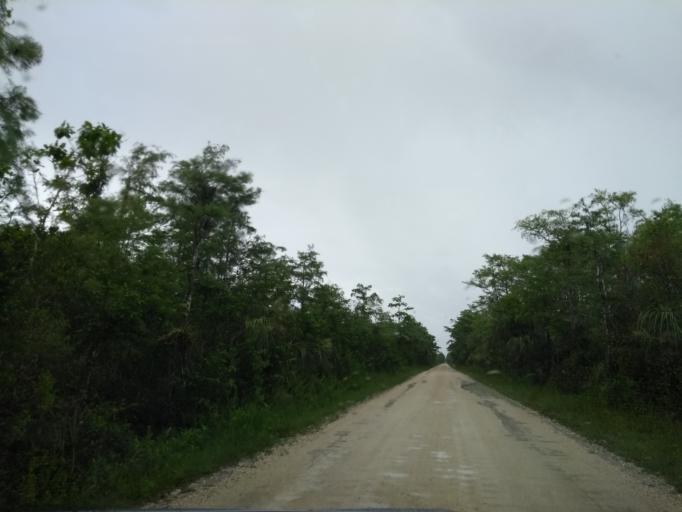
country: US
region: Florida
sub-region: Miami-Dade County
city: The Hammocks
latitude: 25.7602
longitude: -81.0306
